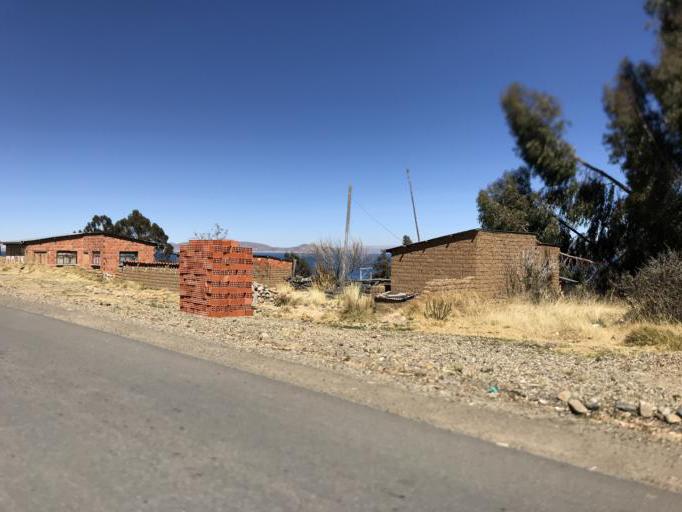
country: BO
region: La Paz
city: Huarina
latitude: -16.2145
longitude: -68.6502
